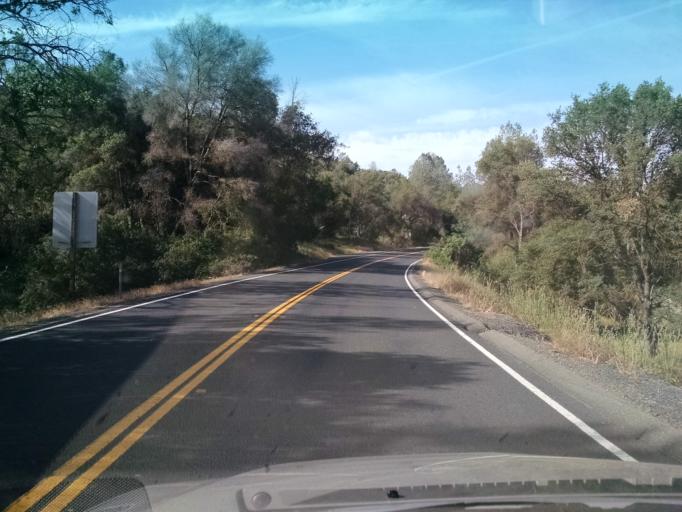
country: US
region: California
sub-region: Madera County
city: Yosemite Lakes
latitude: 37.1938
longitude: -119.7216
